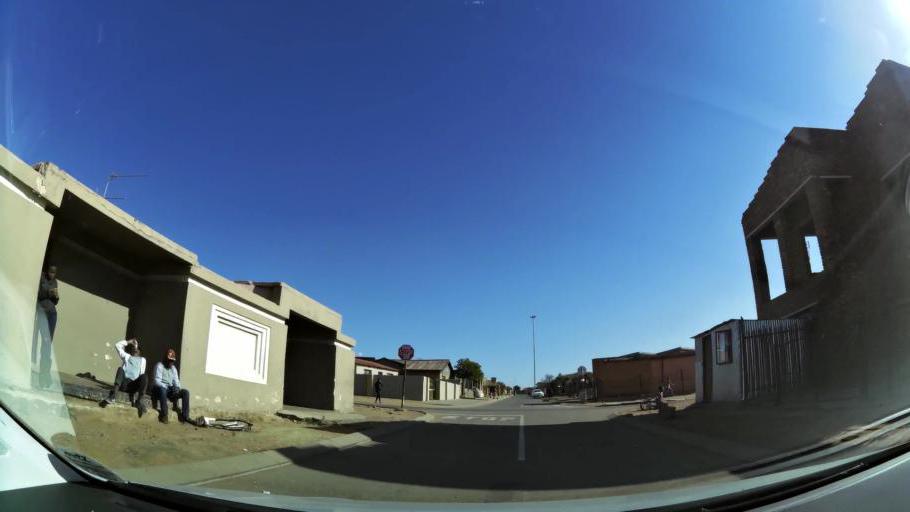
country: ZA
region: Gauteng
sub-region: Ekurhuleni Metropolitan Municipality
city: Tembisa
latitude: -26.0192
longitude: 28.2370
